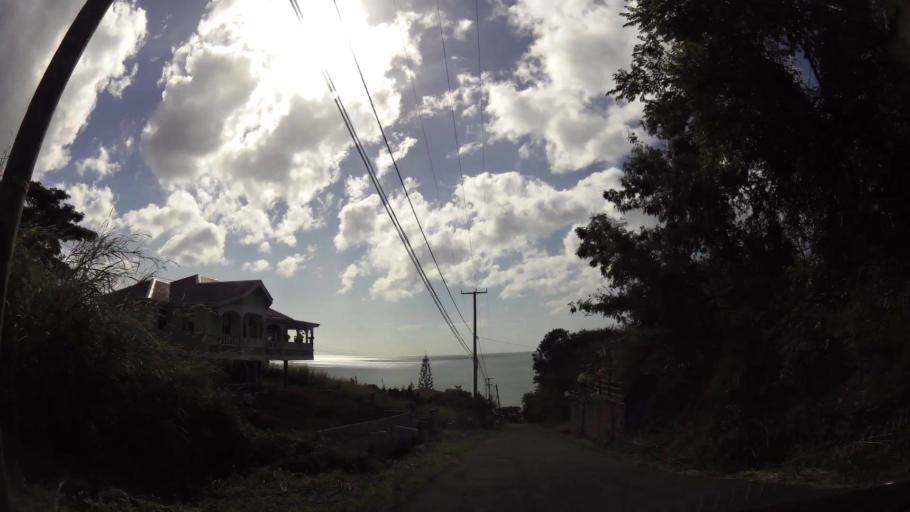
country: DM
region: Saint George
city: Roseau
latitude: 15.2839
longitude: -61.3726
